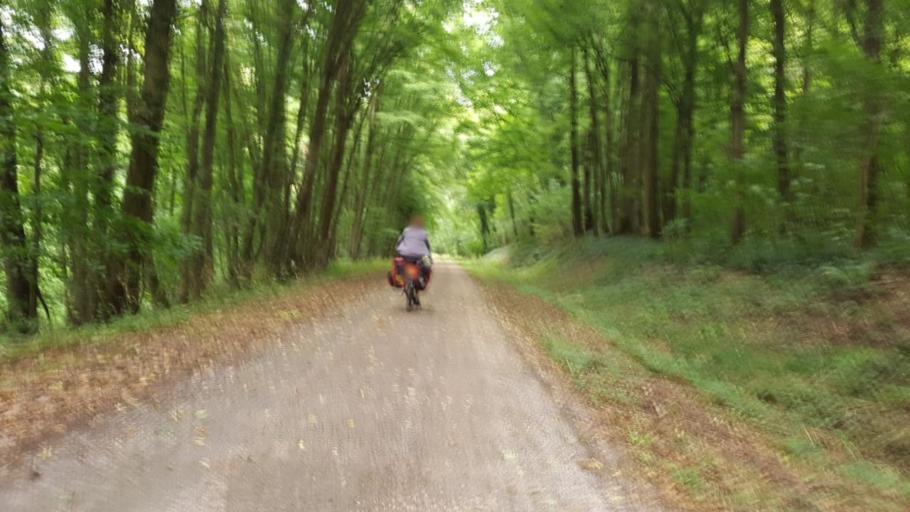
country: FR
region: Picardie
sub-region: Departement de l'Aisne
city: Guise
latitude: 49.8933
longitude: 3.6918
